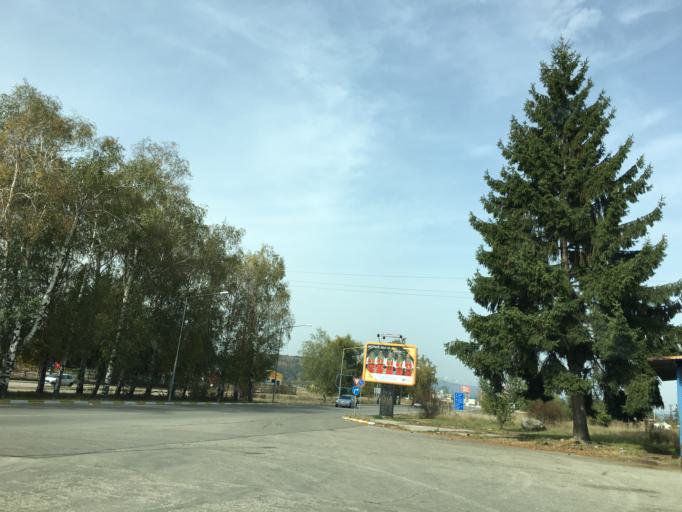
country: BG
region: Sofiya
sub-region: Obshtina Samokov
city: Samokov
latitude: 42.3522
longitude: 23.5496
